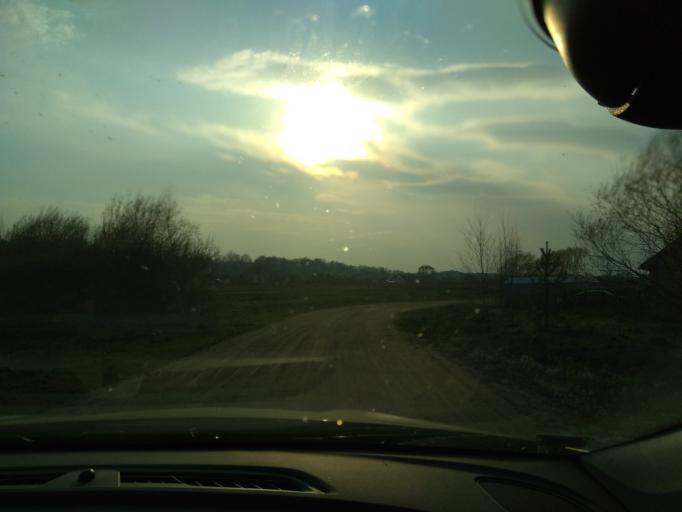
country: LT
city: Baltoji Voke
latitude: 54.5952
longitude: 25.1819
